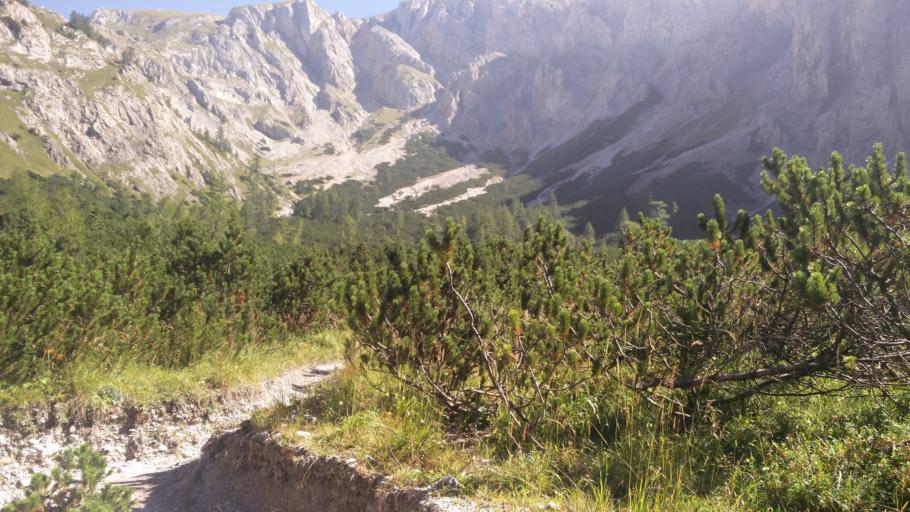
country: AT
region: Styria
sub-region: Politischer Bezirk Bruck-Muerzzuschlag
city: Sankt Ilgen
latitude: 47.6012
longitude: 15.1359
